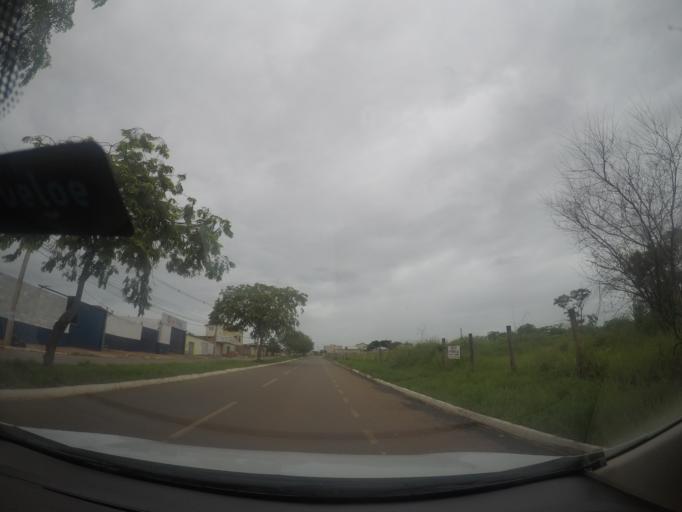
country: BR
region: Goias
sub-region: Goiania
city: Goiania
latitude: -16.6262
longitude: -49.3078
